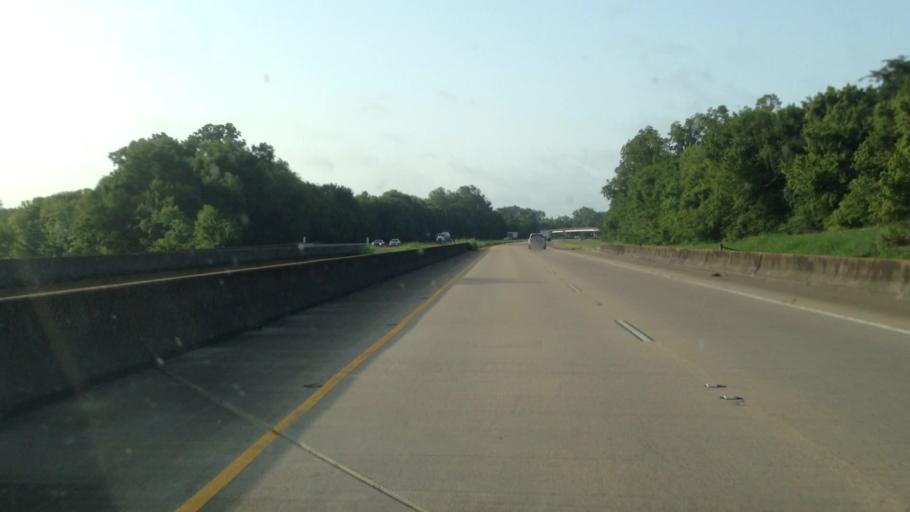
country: US
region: Louisiana
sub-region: Rapides Parish
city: Woodworth
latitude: 31.1328
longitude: -92.4464
